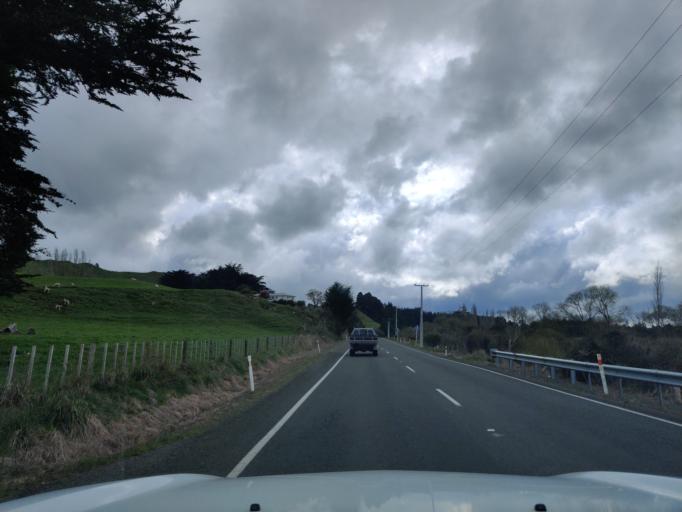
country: NZ
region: Manawatu-Wanganui
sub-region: Ruapehu District
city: Waiouru
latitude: -39.4450
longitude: 175.2896
